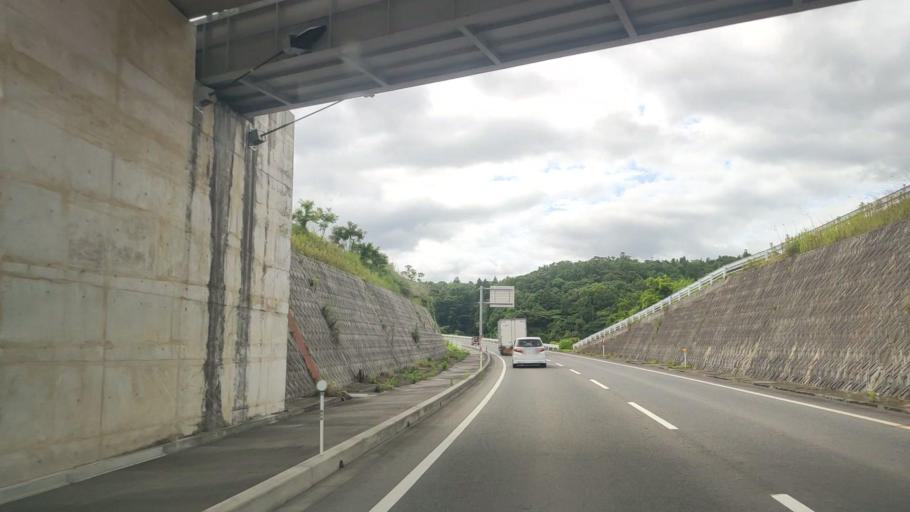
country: JP
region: Tottori
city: Yonago
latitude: 35.3813
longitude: 133.3880
